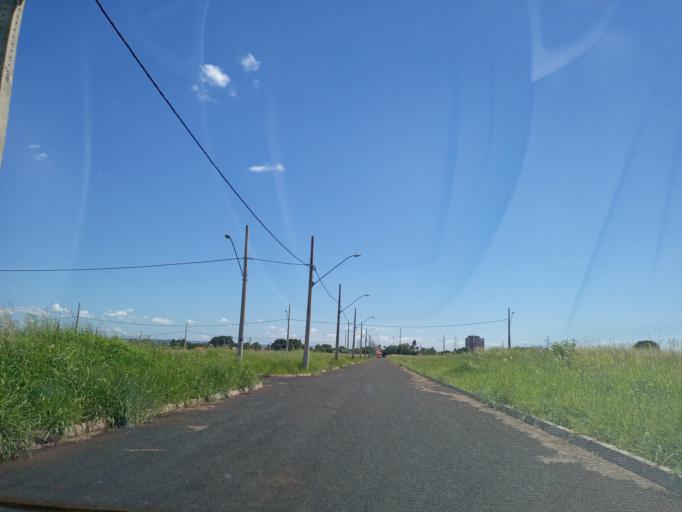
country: BR
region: Minas Gerais
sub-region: Centralina
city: Centralina
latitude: -18.5984
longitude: -49.1971
